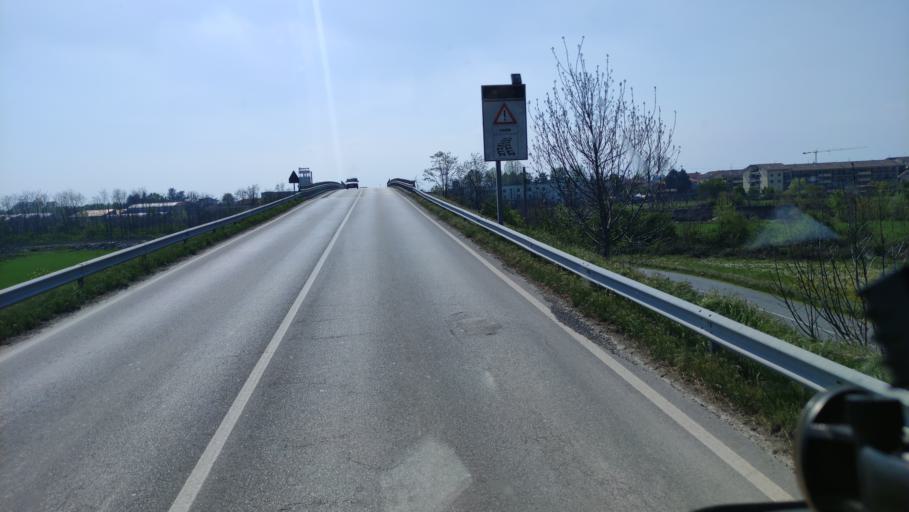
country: IT
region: Piedmont
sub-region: Provincia di Cuneo
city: Savigliano
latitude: 44.6393
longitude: 7.6681
